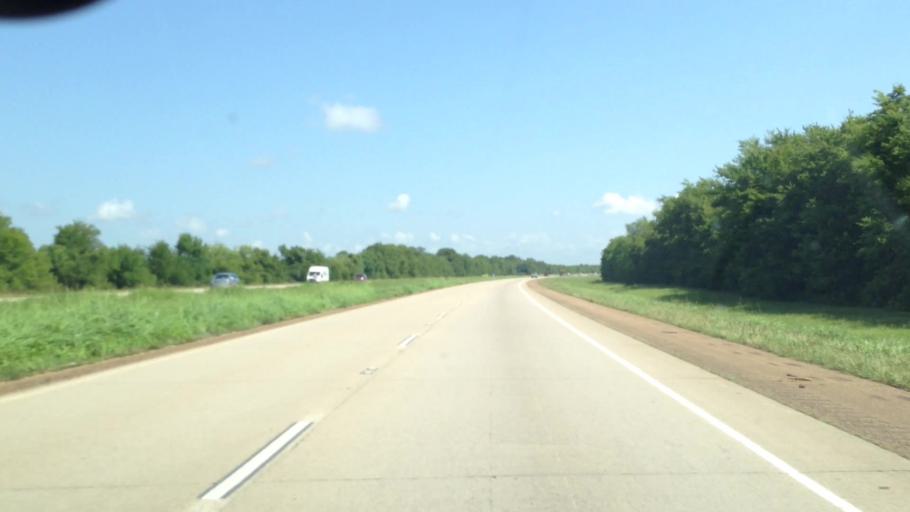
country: US
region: Louisiana
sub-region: Rapides Parish
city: Woodworth
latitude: 31.1915
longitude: -92.4734
